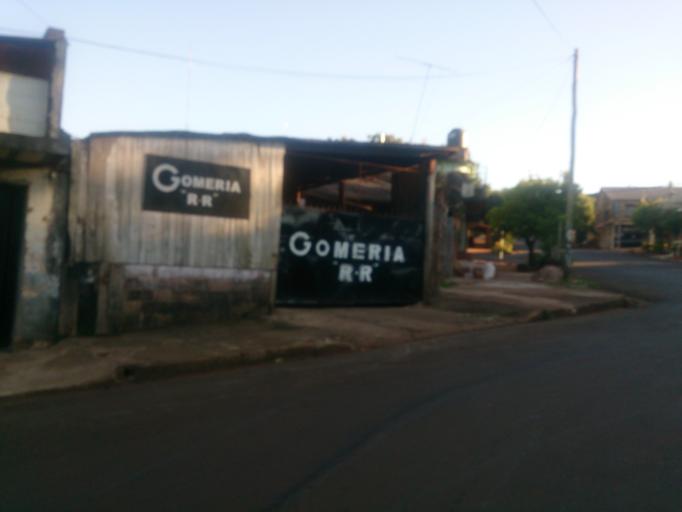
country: AR
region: Misiones
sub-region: Departamento de Obera
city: Obera
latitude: -27.4902
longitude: -55.1182
